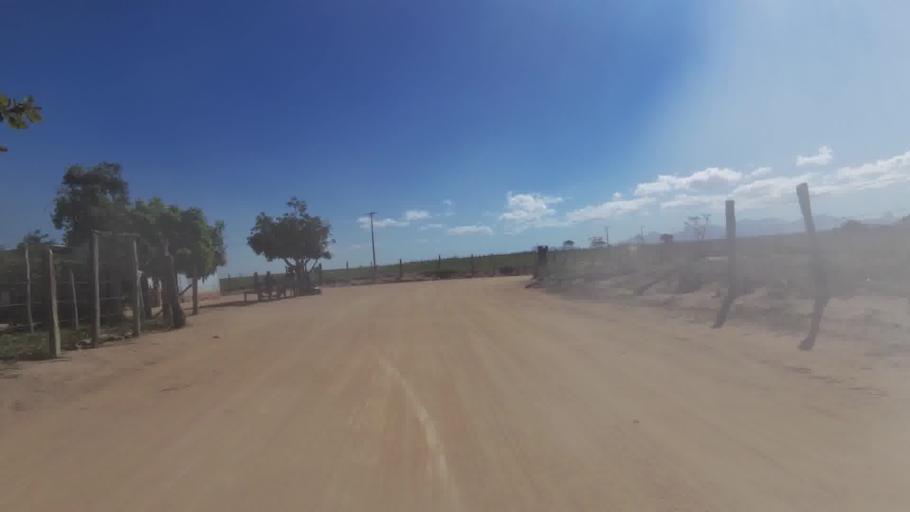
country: BR
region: Espirito Santo
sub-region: Marataizes
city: Marataizes
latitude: -21.1574
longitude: -40.9773
